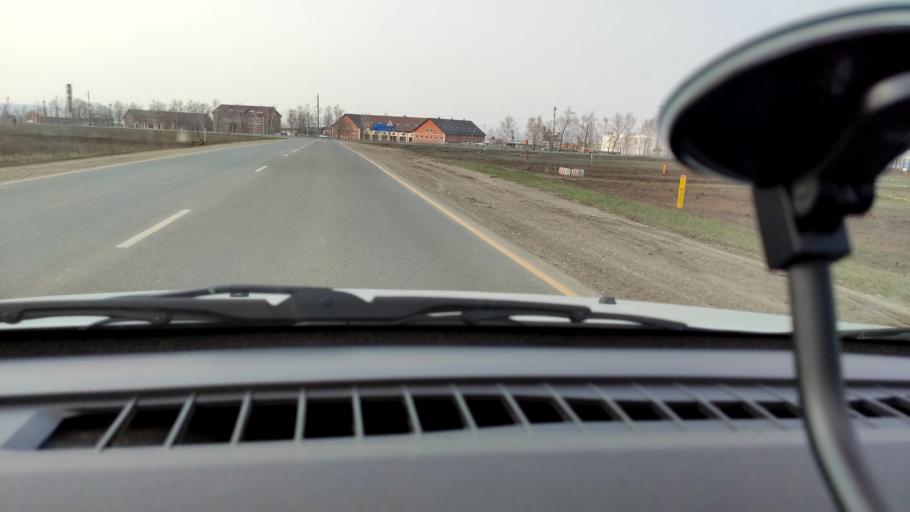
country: RU
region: Samara
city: Dubovyy Umet
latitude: 53.0821
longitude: 50.3458
